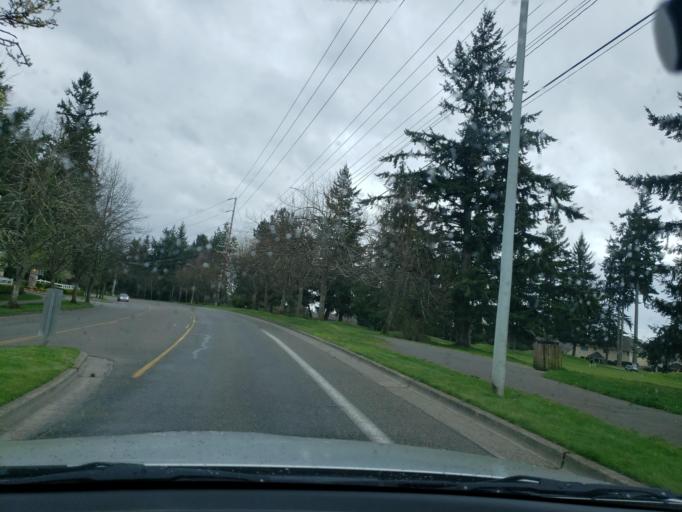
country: US
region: Washington
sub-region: Snohomish County
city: Meadowdale
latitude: 47.8930
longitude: -122.3121
